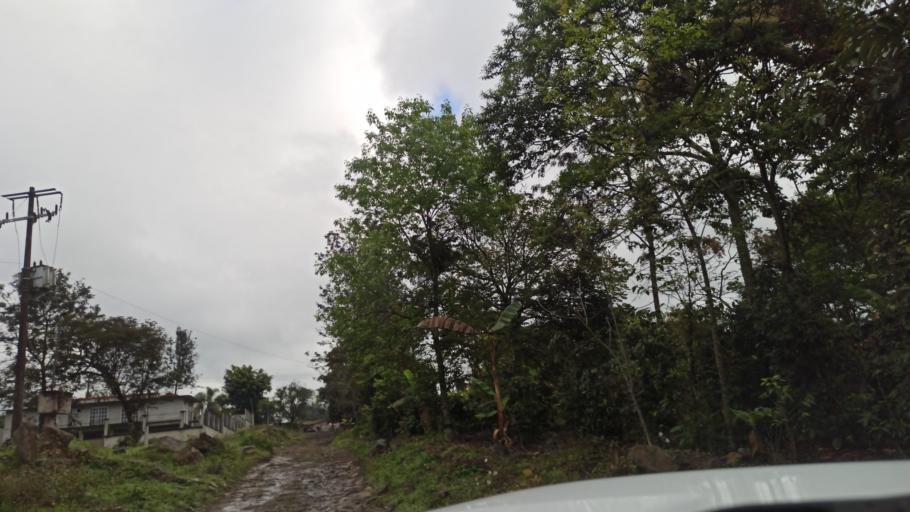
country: MX
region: Veracruz
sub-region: Chocaman
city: San Jose Neria
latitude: 19.0040
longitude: -97.0084
